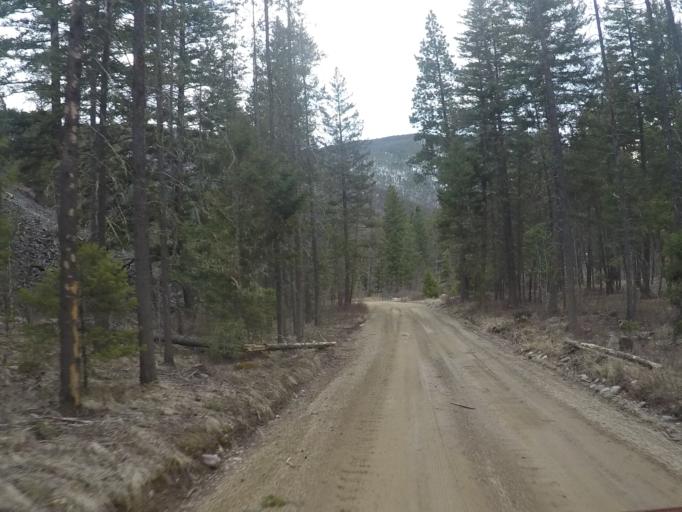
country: US
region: Montana
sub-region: Missoula County
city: Clinton
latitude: 46.5667
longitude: -113.6998
